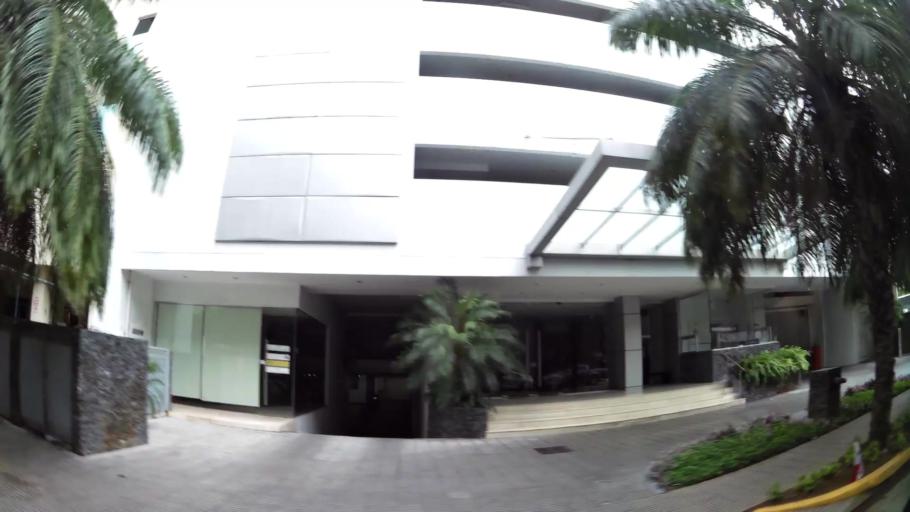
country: PA
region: Panama
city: Panama
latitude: 8.9766
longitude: -79.5210
